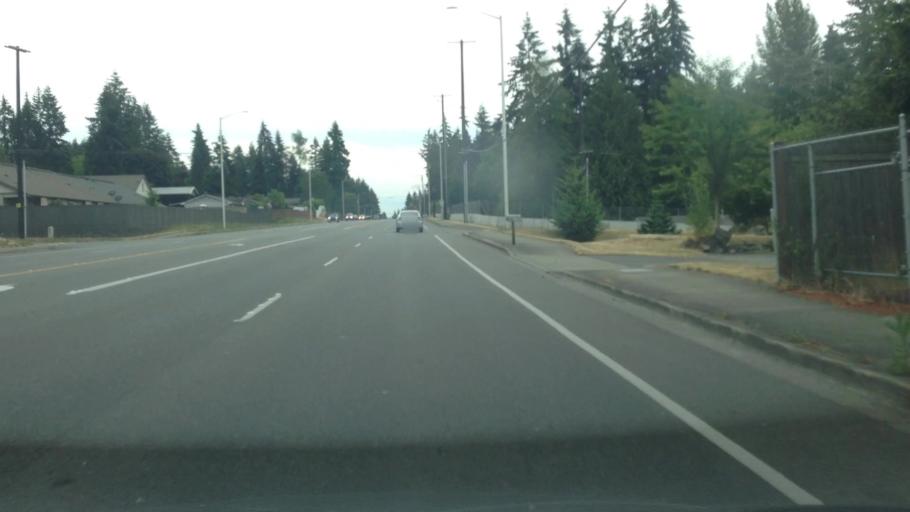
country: US
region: Washington
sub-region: Pierce County
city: South Hill
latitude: 47.1499
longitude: -122.3040
